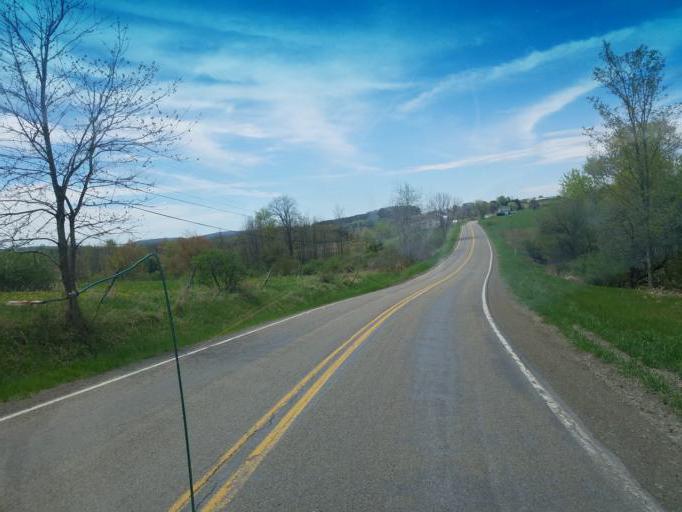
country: US
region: Pennsylvania
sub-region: Tioga County
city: Wellsboro
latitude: 41.7141
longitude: -77.3818
